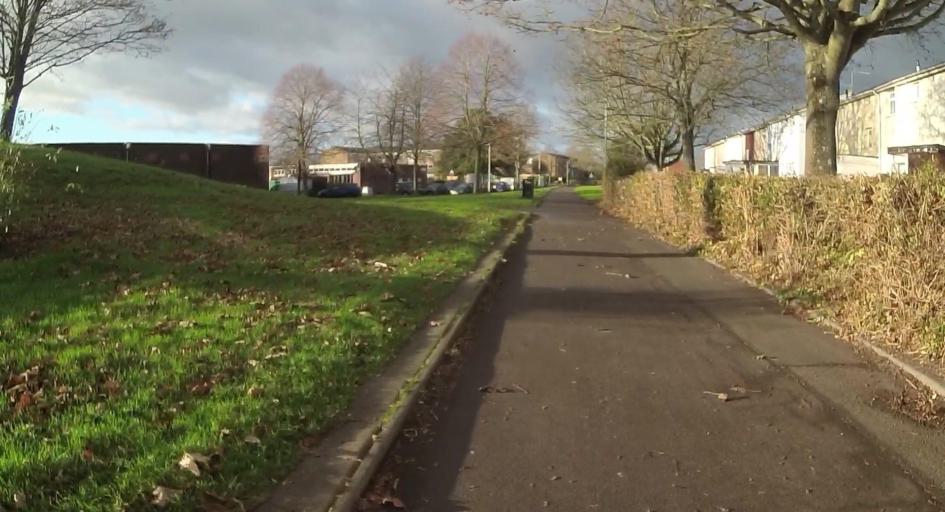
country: GB
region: England
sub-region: Bracknell Forest
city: Bracknell
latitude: 51.3992
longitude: -0.7685
